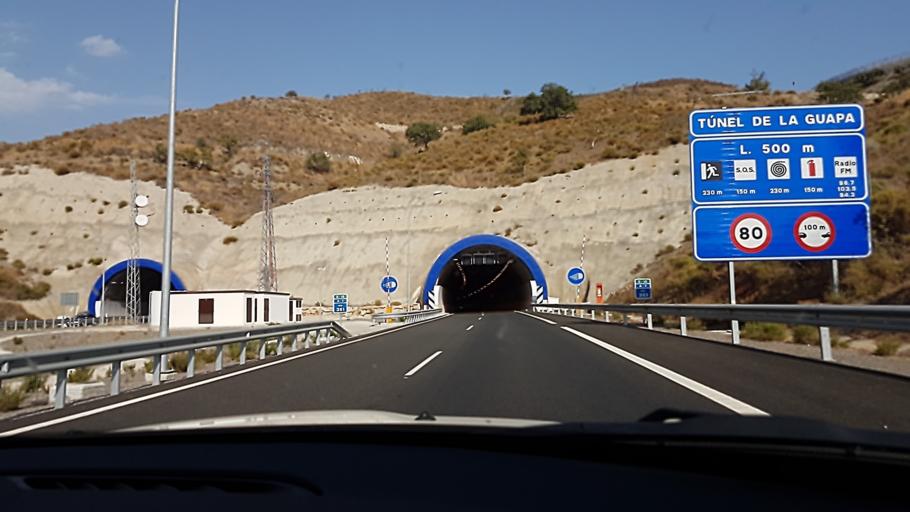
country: ES
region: Andalusia
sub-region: Provincia de Granada
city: Polopos
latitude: 36.7505
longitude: -3.3014
